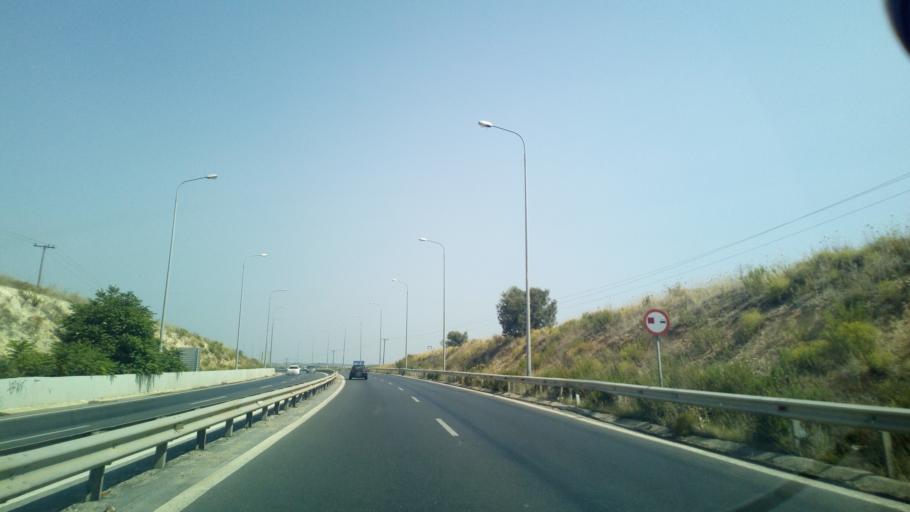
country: GR
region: Central Macedonia
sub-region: Nomos Chalkidikis
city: Nea Plagia
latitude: 40.2850
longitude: 23.1518
